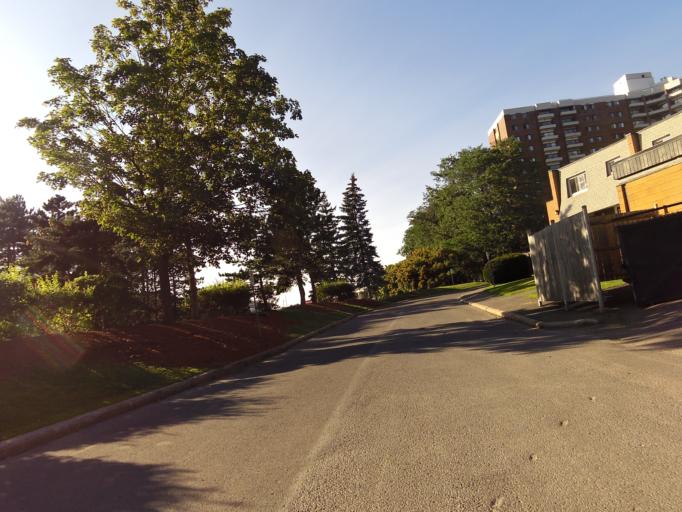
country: CA
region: Ontario
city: Ottawa
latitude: 45.3506
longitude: -75.7293
